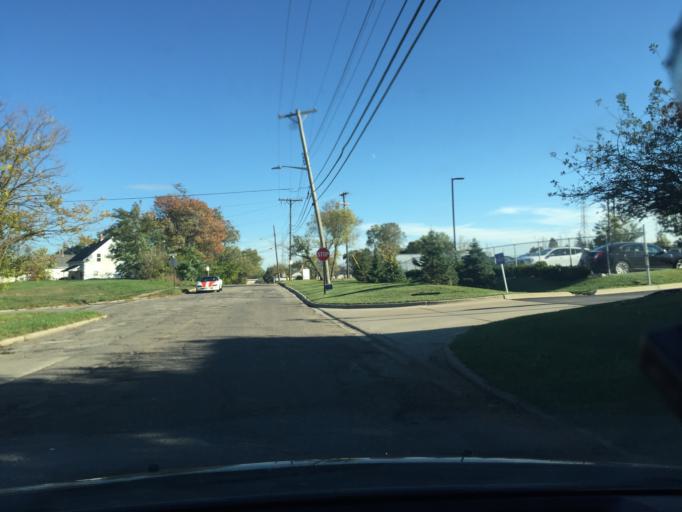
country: US
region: Michigan
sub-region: Oakland County
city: Pontiac
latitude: 42.6221
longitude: -83.2788
